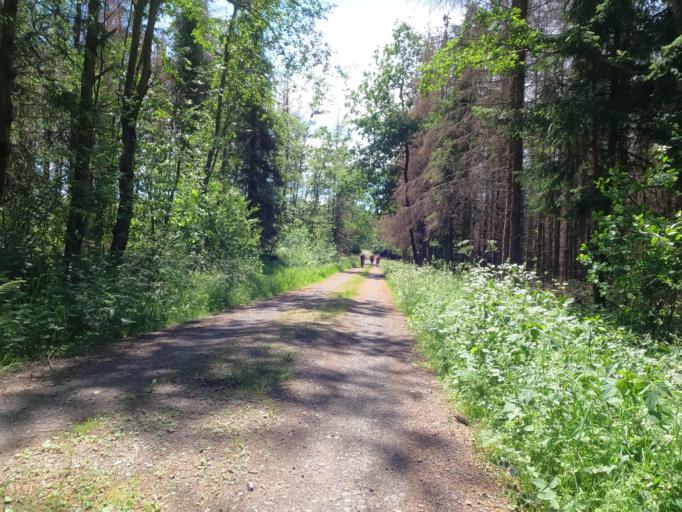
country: DE
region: Rheinland-Pfalz
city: Alpenrod
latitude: 50.6420
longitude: 7.8534
